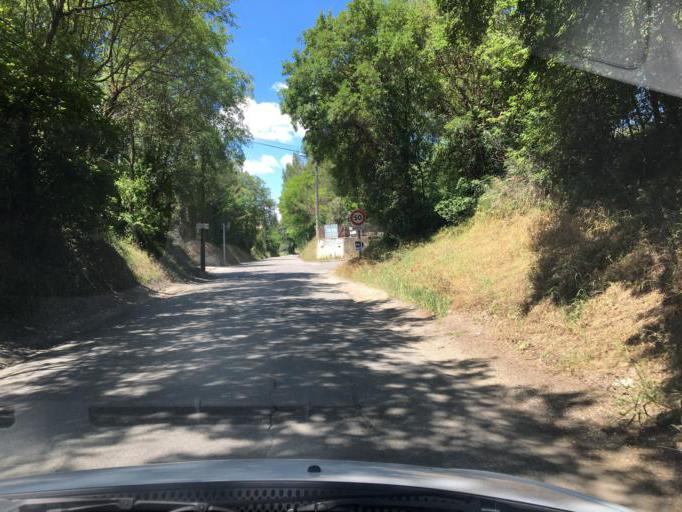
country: FR
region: Provence-Alpes-Cote d'Azur
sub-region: Departement du Vaucluse
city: Carpentras
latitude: 44.0514
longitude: 5.0627
